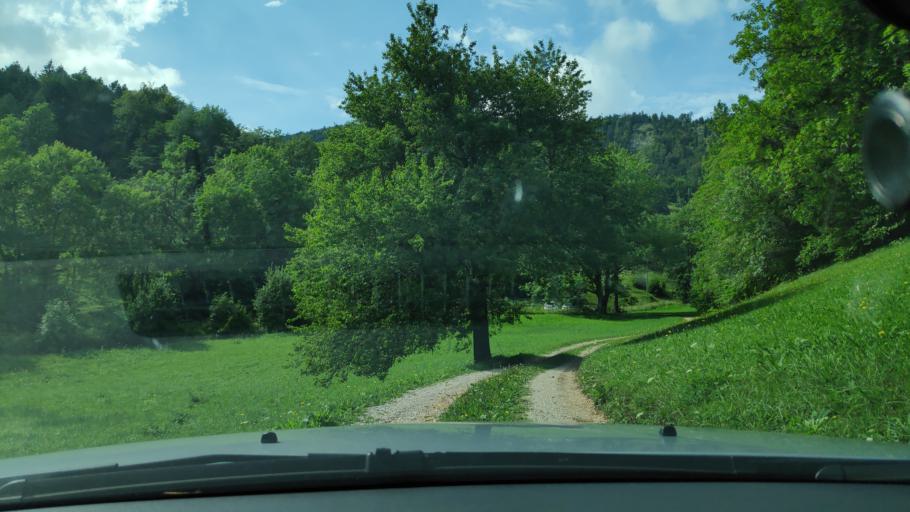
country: AT
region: Lower Austria
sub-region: Politischer Bezirk Wiener Neustadt
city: Miesenbach
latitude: 47.8366
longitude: 15.9557
